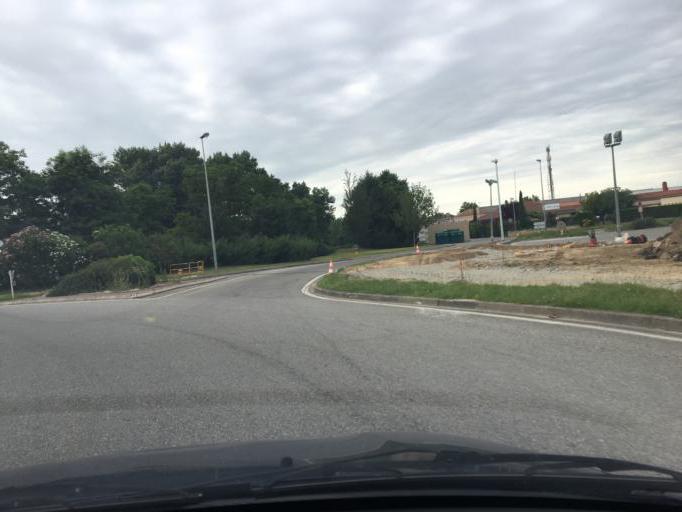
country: FR
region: Rhone-Alpes
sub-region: Departement de l'Ardeche
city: Guilherand-Granges
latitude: 44.9398
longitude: 4.8658
